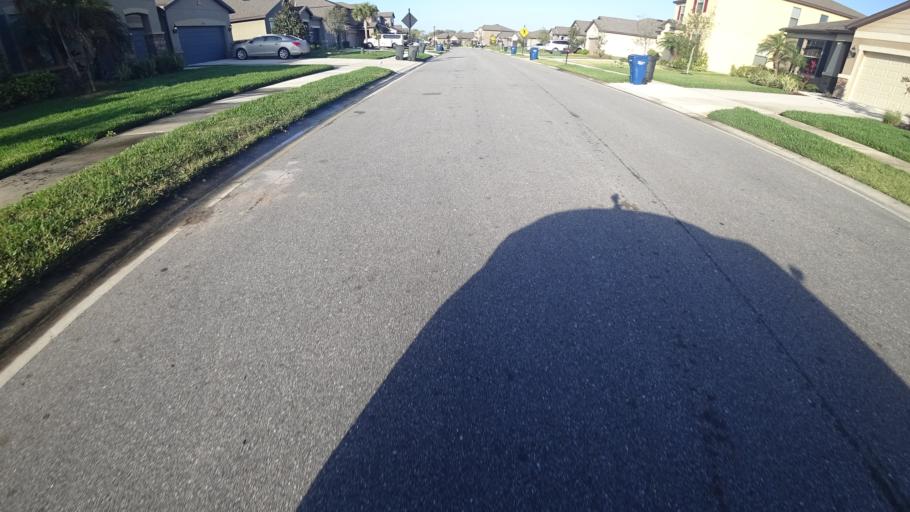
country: US
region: Florida
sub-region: Manatee County
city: Ellenton
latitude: 27.5686
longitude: -82.4490
